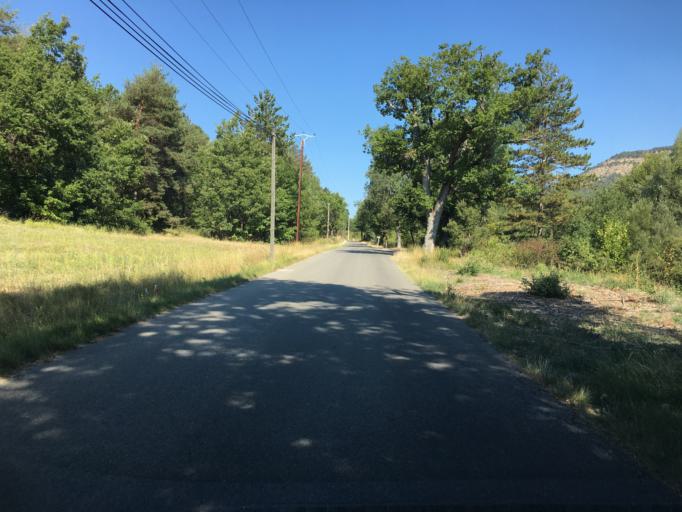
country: FR
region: Provence-Alpes-Cote d'Azur
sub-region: Departement des Alpes-de-Haute-Provence
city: Mallemoisson
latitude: 44.0626
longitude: 6.1474
